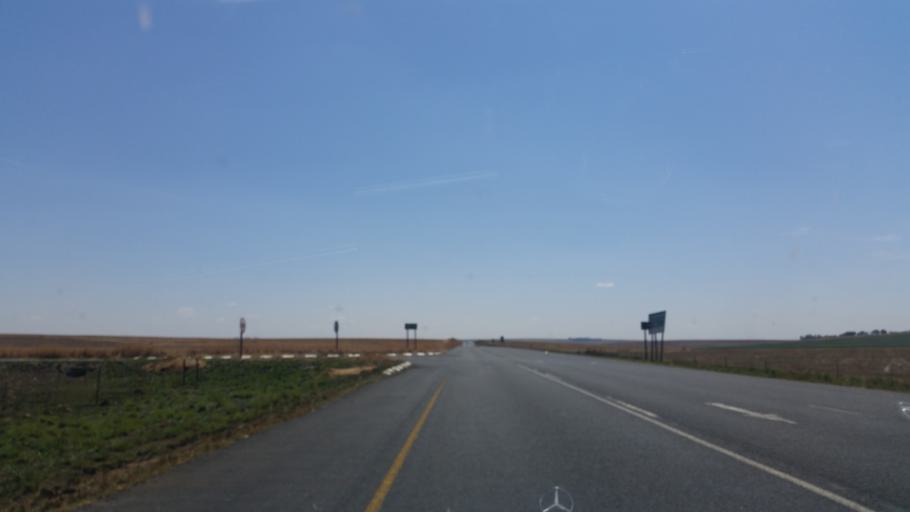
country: ZA
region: Orange Free State
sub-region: Thabo Mofutsanyana District Municipality
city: Bethlehem
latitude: -28.1619
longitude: 28.6828
